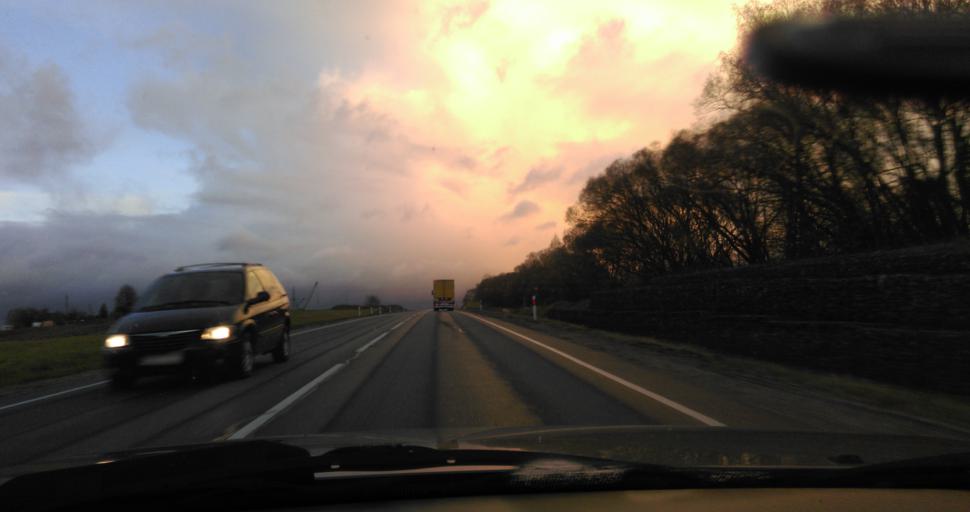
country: LT
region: Utenos apskritis
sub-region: Utena
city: Utena
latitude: 55.5187
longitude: 25.6590
